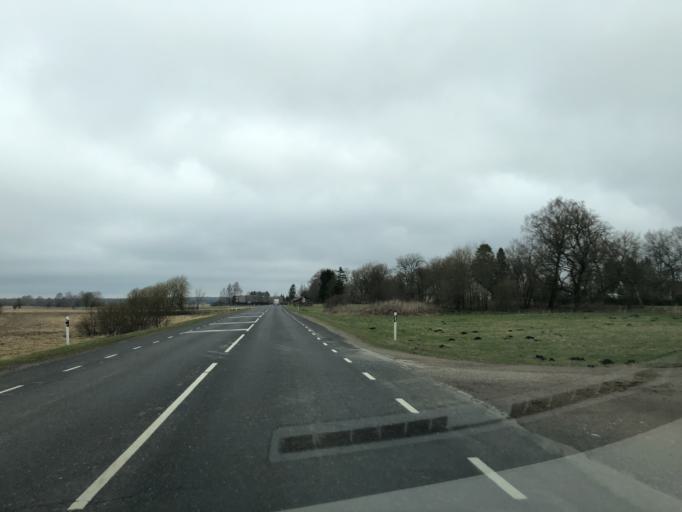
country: EE
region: Laeaene-Virumaa
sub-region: Vaeike-Maarja vald
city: Vaike-Maarja
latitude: 59.2263
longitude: 26.2637
